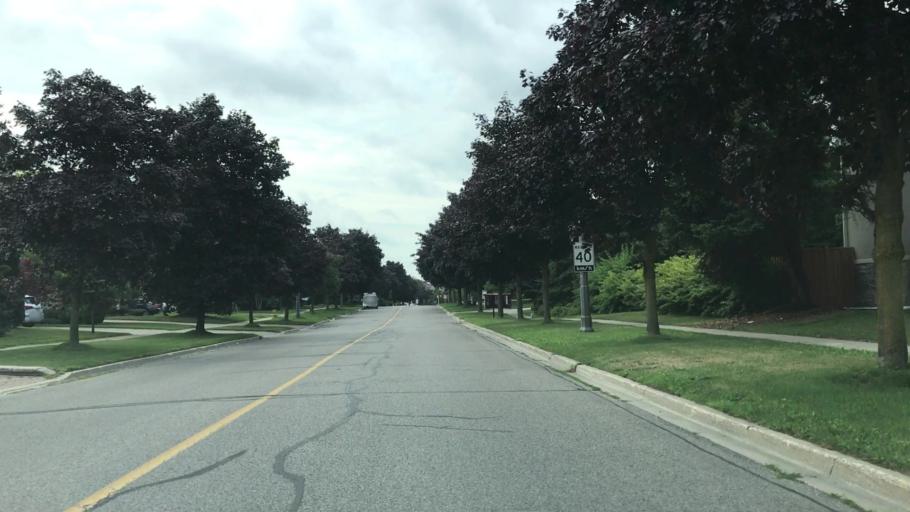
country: CA
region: Ontario
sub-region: York
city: Richmond Hill
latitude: 43.8610
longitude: -79.4041
